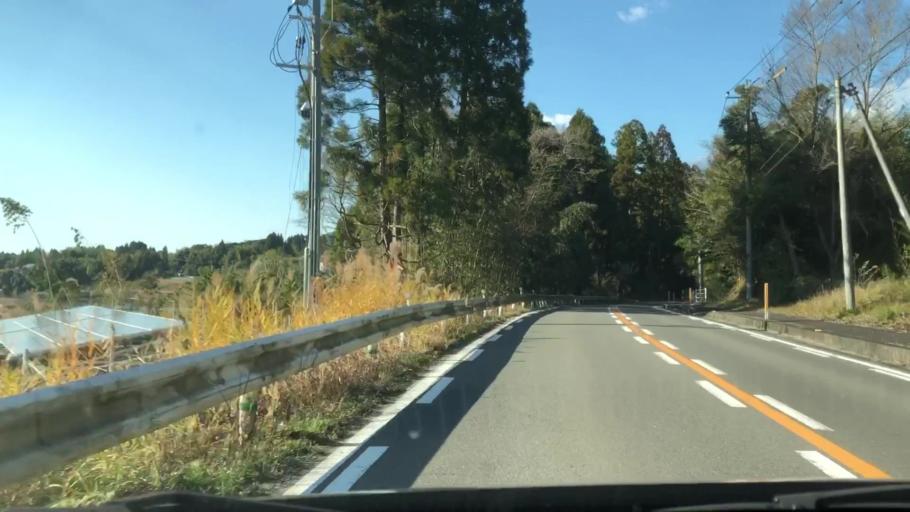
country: JP
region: Kagoshima
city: Satsumasendai
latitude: 31.8571
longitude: 130.3727
